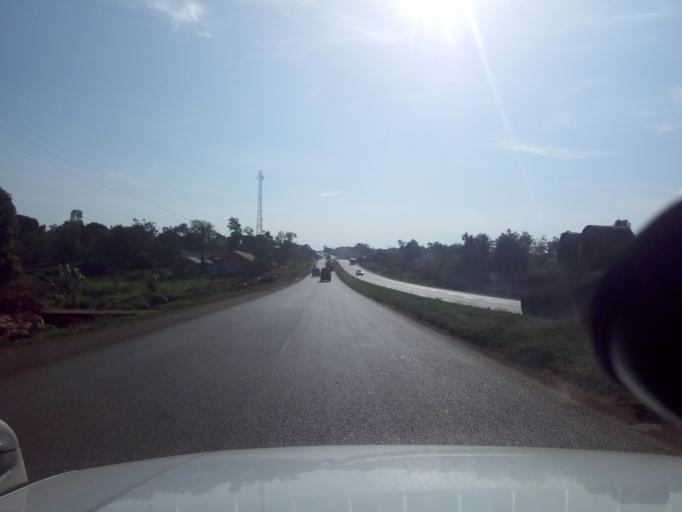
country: UG
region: Eastern Region
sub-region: Jinja District
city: Bugembe
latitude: 0.4747
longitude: 33.2610
